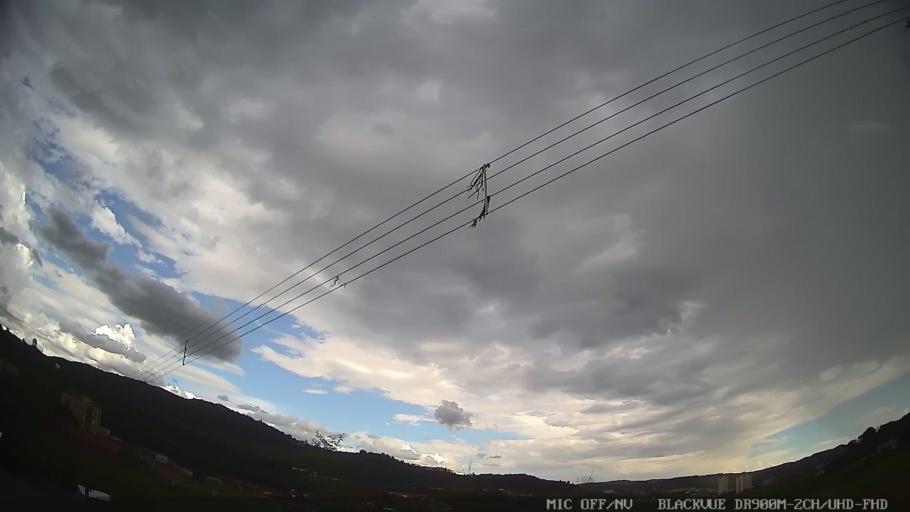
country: BR
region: Sao Paulo
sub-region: Pedreira
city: Pedreira
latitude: -22.7149
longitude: -46.8961
